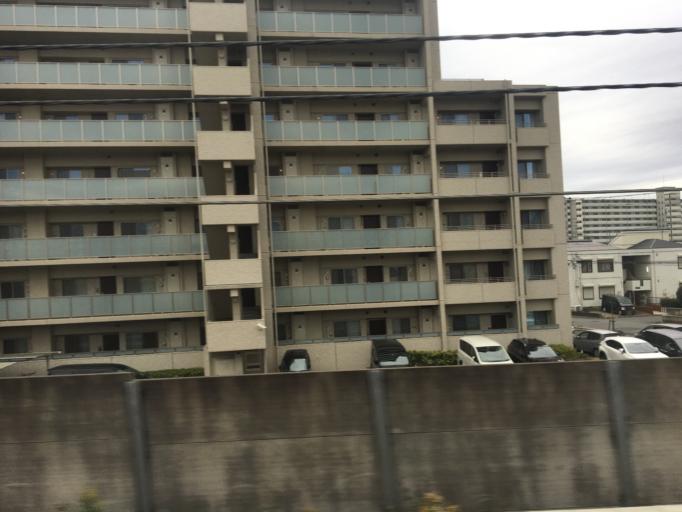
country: JP
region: Chiba
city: Nagareyama
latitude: 35.8294
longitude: 139.9135
